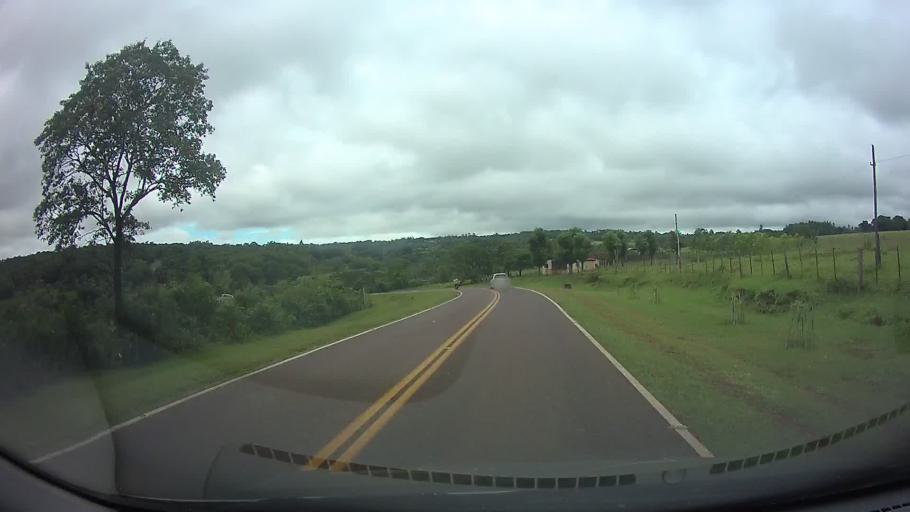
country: PY
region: Paraguari
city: Acahay
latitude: -25.9260
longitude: -57.1079
